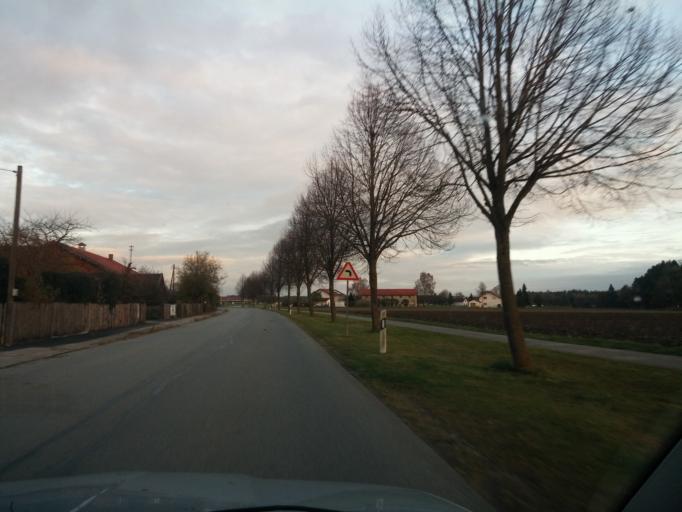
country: DE
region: Bavaria
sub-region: Upper Bavaria
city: Forstinning
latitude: 48.1690
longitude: 11.9269
